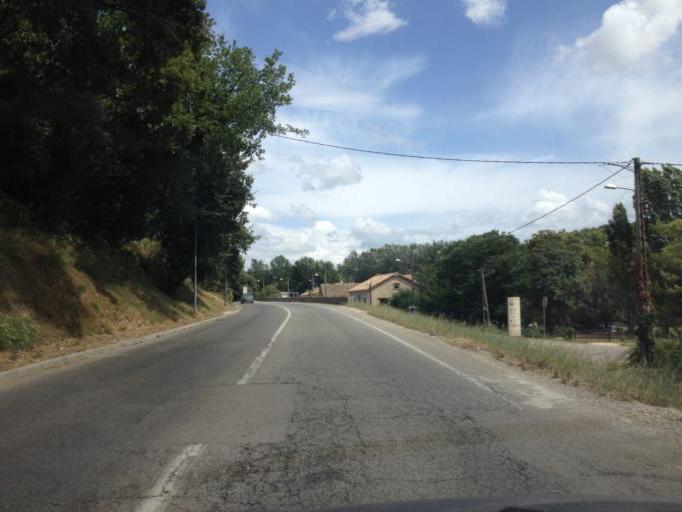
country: FR
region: Provence-Alpes-Cote d'Azur
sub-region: Departement du Vaucluse
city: Vaison-la-Romaine
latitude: 44.2382
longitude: 5.0581
